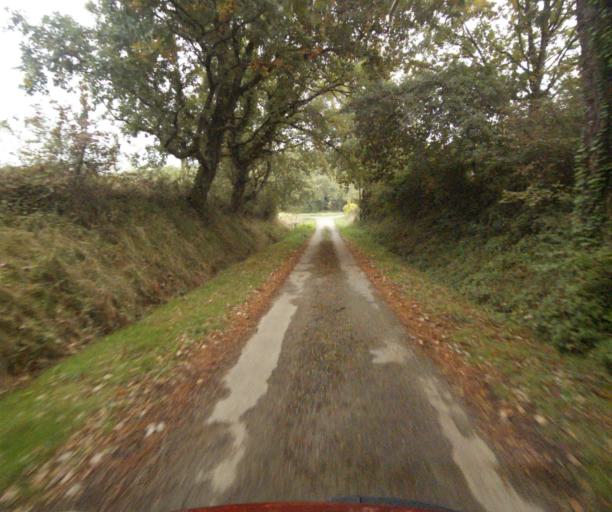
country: FR
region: Midi-Pyrenees
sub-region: Departement du Tarn-et-Garonne
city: Verdun-sur-Garonne
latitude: 43.8336
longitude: 1.1912
